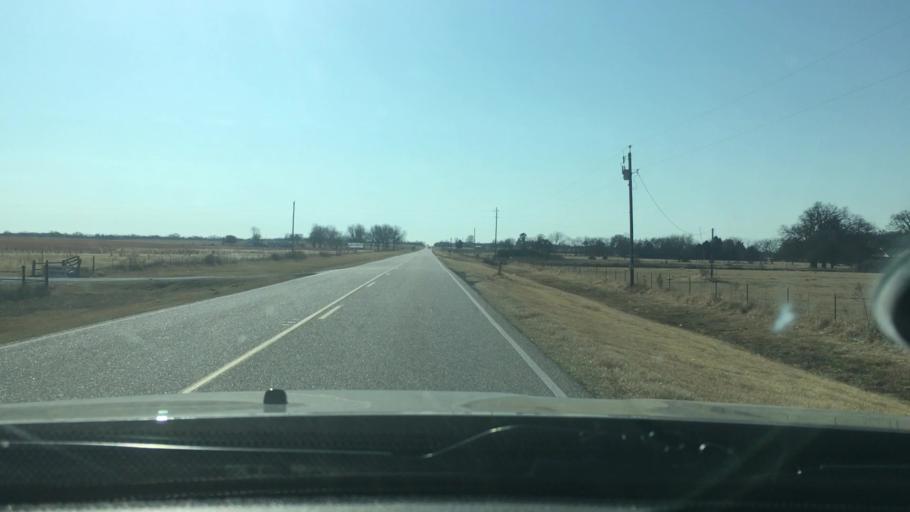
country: US
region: Oklahoma
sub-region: Garvin County
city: Stratford
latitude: 34.8487
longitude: -96.9677
